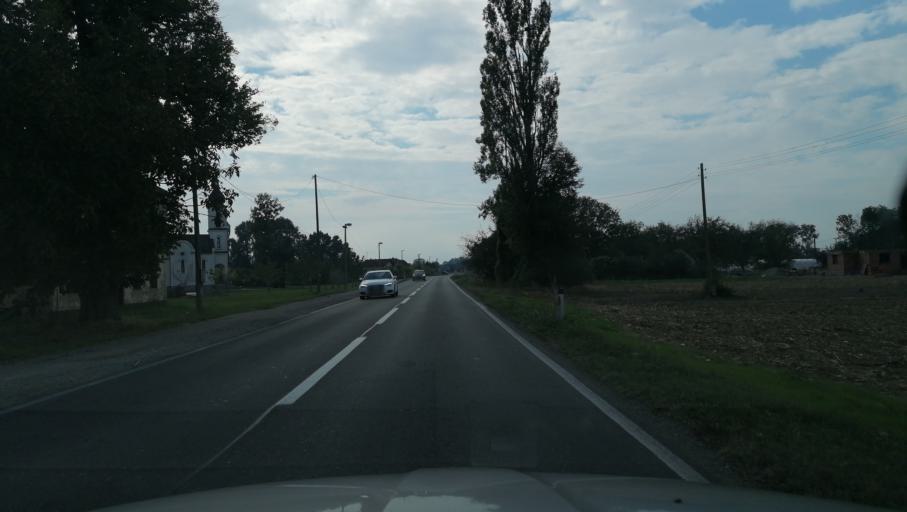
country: BA
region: Republika Srpska
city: Dvorovi
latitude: 44.8272
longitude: 19.2864
